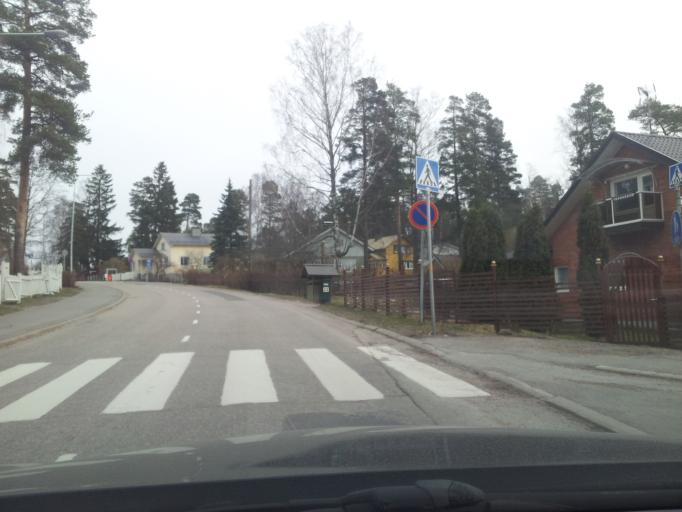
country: FI
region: Uusimaa
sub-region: Helsinki
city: Kilo
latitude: 60.2024
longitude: 24.8051
